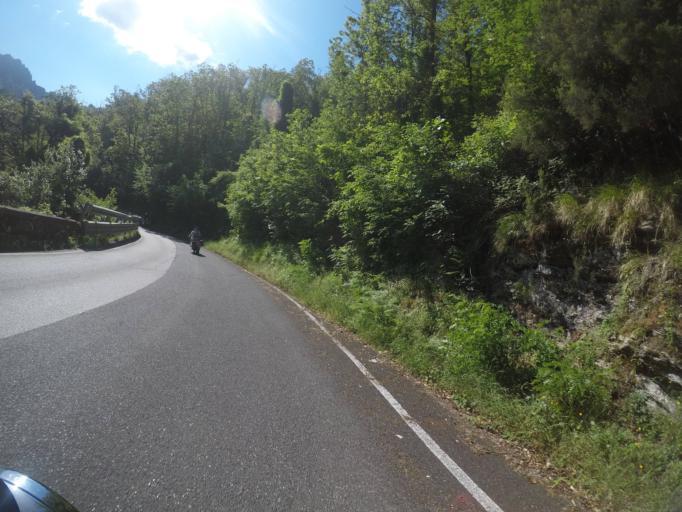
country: IT
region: Tuscany
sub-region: Provincia di Massa-Carrara
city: Montignoso
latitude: 44.0526
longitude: 10.1776
